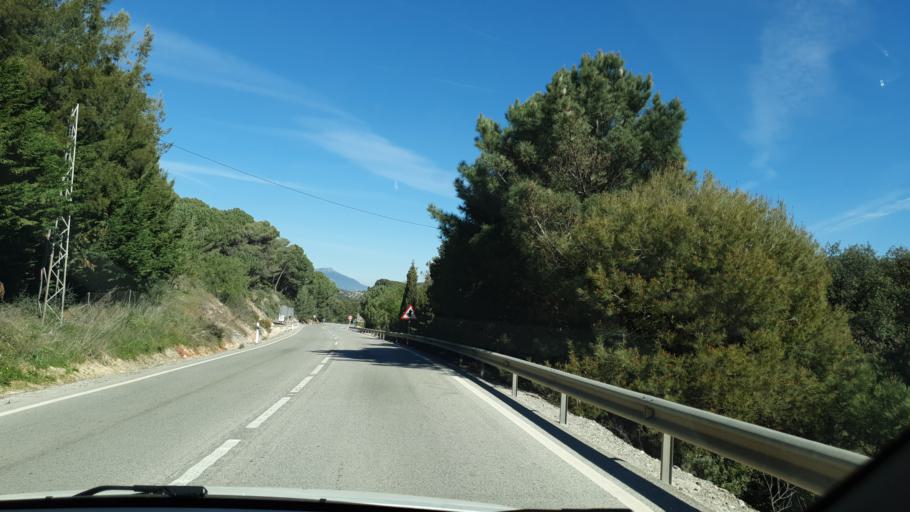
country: ES
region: Andalusia
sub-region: Provincia de Malaga
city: Ojen
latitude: 36.5876
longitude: -4.8521
